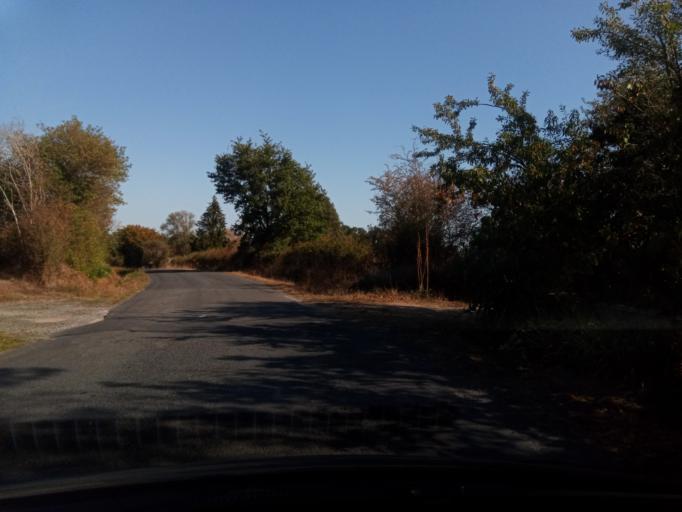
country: FR
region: Poitou-Charentes
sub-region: Departement de la Vienne
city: Saulge
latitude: 46.3365
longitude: 0.8745
